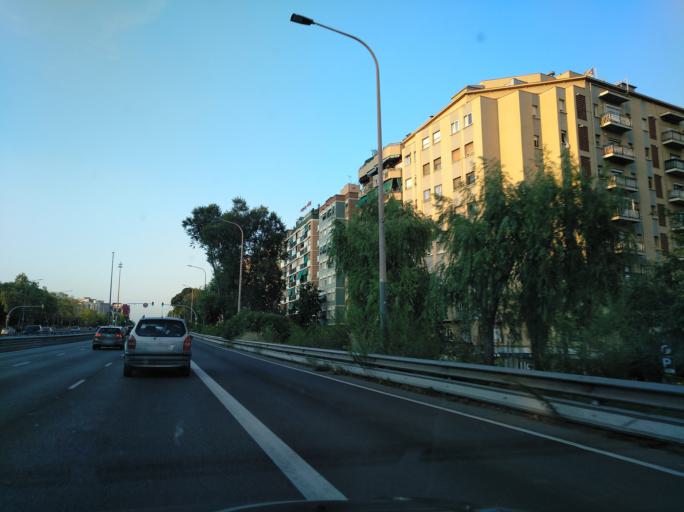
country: ES
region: Catalonia
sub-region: Provincia de Barcelona
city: Sant Andreu de Palomar
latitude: 41.4354
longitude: 2.1841
